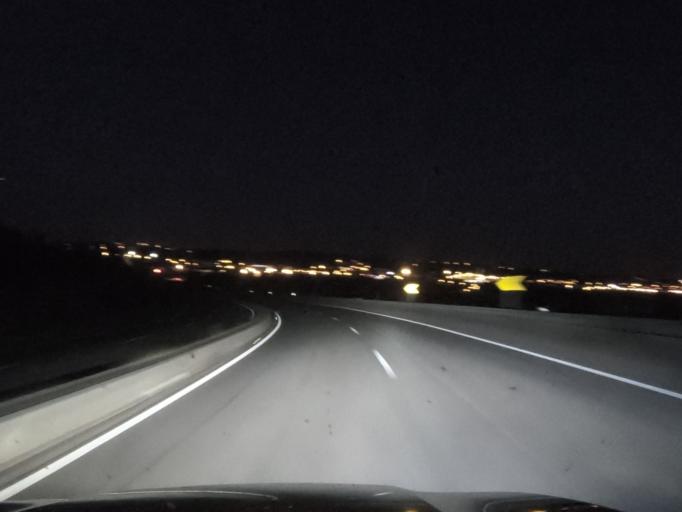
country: PT
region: Faro
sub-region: Loule
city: Loule
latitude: 37.1379
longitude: -8.0444
